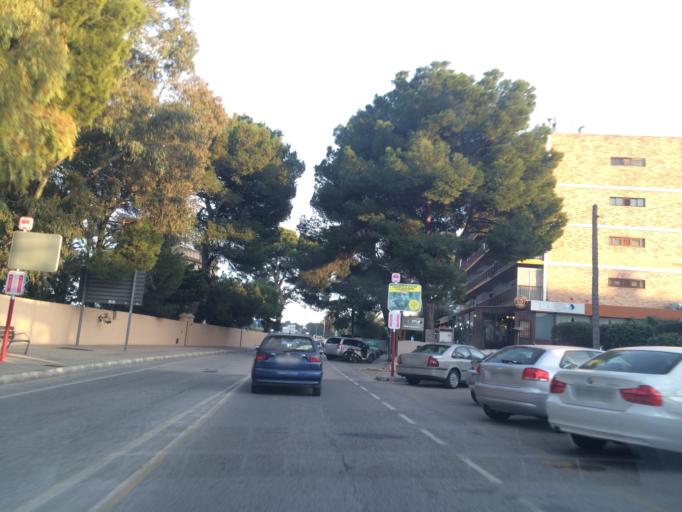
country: ES
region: Valencia
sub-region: Provincia de Alicante
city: Denia
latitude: 38.8346
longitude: 0.1211
